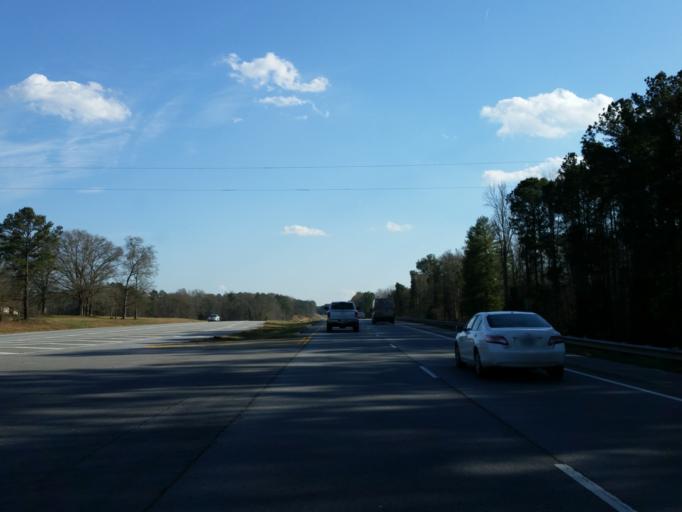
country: US
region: Georgia
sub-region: Spalding County
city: Griffin
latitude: 33.1615
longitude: -84.2569
